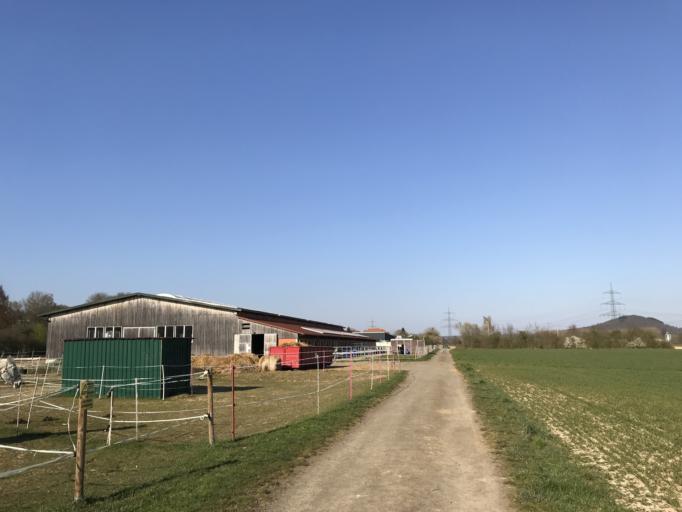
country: DE
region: Hesse
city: Lollar
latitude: 50.6273
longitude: 8.6752
